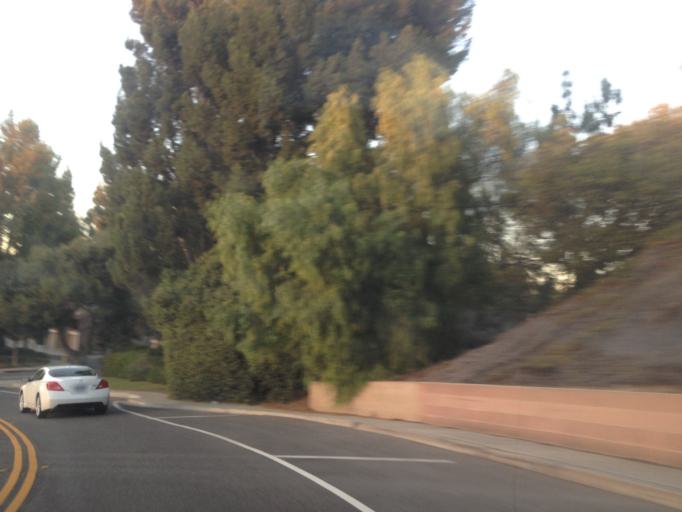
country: US
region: California
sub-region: Orange County
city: Fullerton
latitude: 33.8854
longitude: -117.9202
